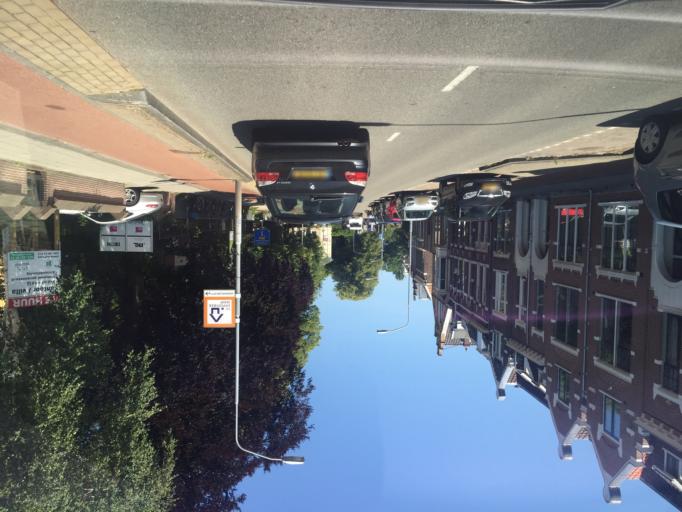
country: NL
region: North Holland
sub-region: Gemeente Haarlem
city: Haarlem
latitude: 52.3881
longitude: 4.6432
